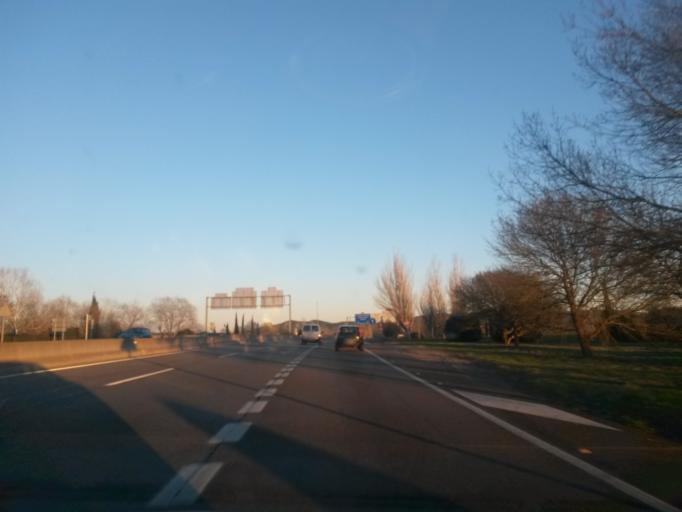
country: ES
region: Catalonia
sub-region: Provincia de Girona
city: Macanet de la Selva
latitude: 41.7860
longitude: 2.7556
